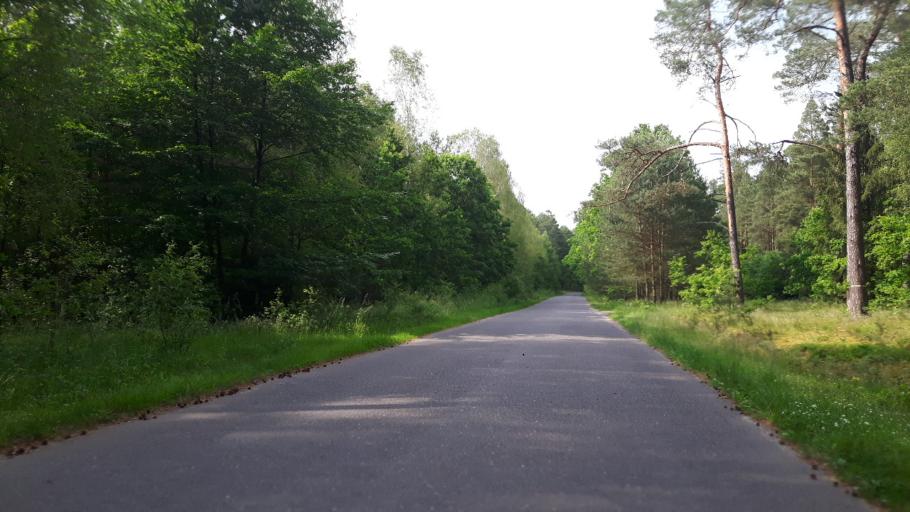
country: PL
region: West Pomeranian Voivodeship
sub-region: Powiat goleniowski
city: Nowogard
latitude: 53.8014
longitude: 15.1275
